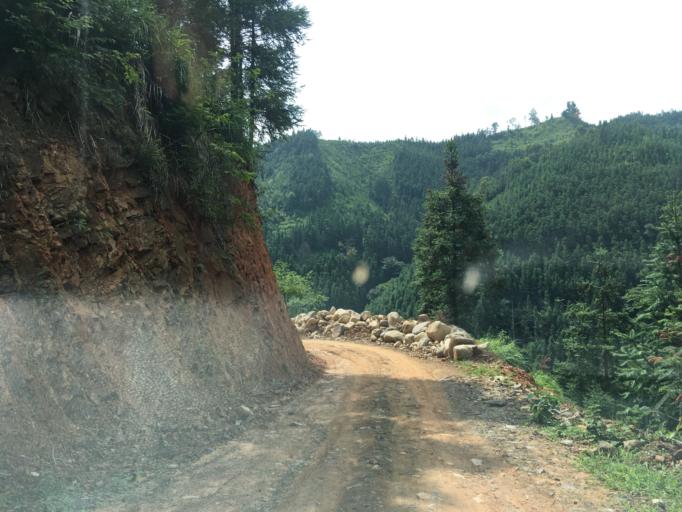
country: CN
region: Guangxi Zhuangzu Zizhiqu
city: Xinzhou
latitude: 24.8664
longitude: 105.8557
